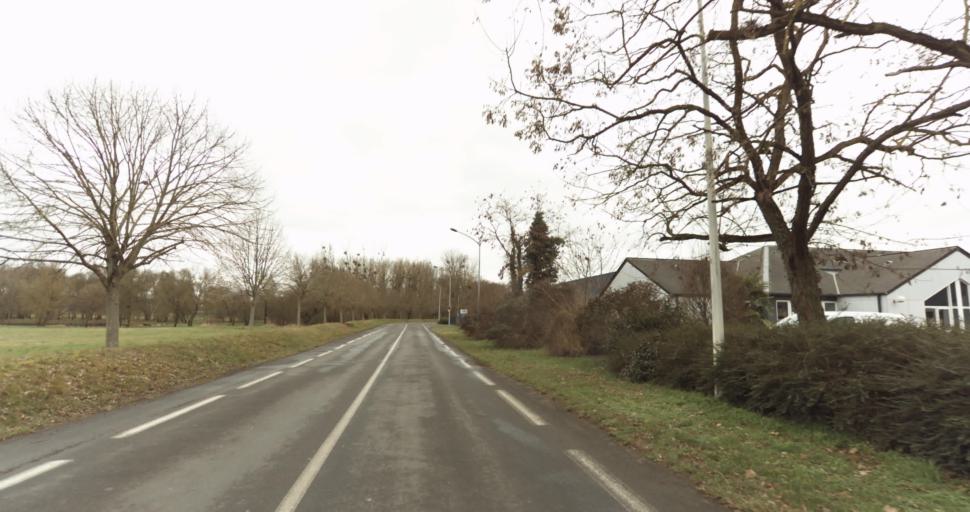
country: FR
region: Pays de la Loire
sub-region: Departement de Maine-et-Loire
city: Saumur
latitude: 47.2501
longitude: -0.0862
